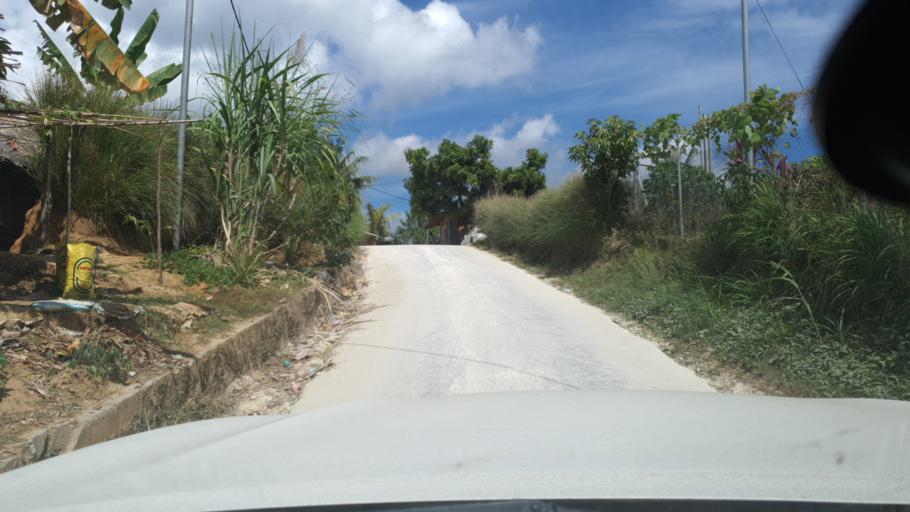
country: SB
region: Guadalcanal
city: Honiara
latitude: -9.4352
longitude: 159.9248
